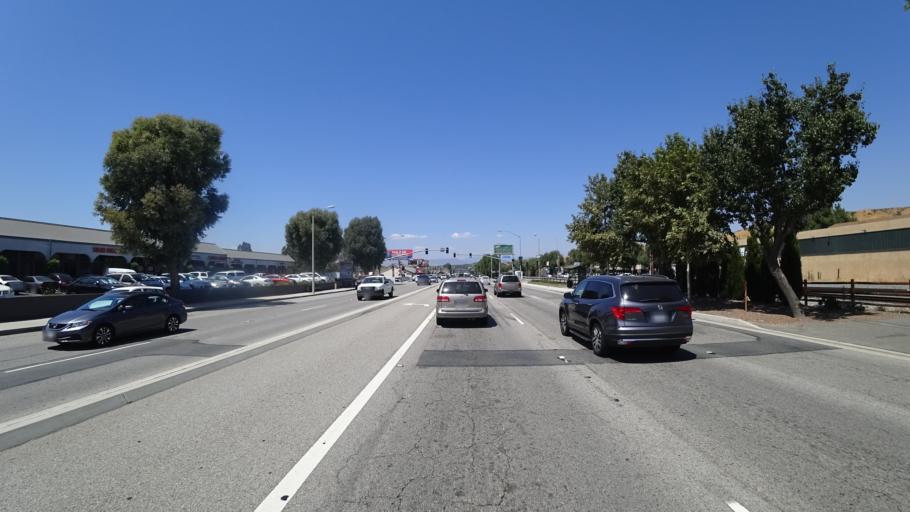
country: US
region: California
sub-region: Los Angeles County
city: Santa Clarita
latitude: 34.4106
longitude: -118.5404
